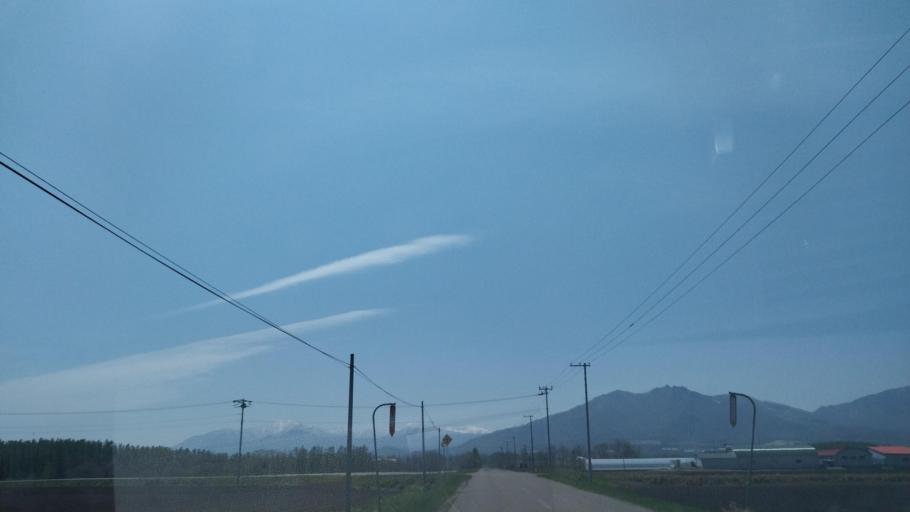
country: JP
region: Hokkaido
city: Obihiro
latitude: 42.9013
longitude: 142.9833
